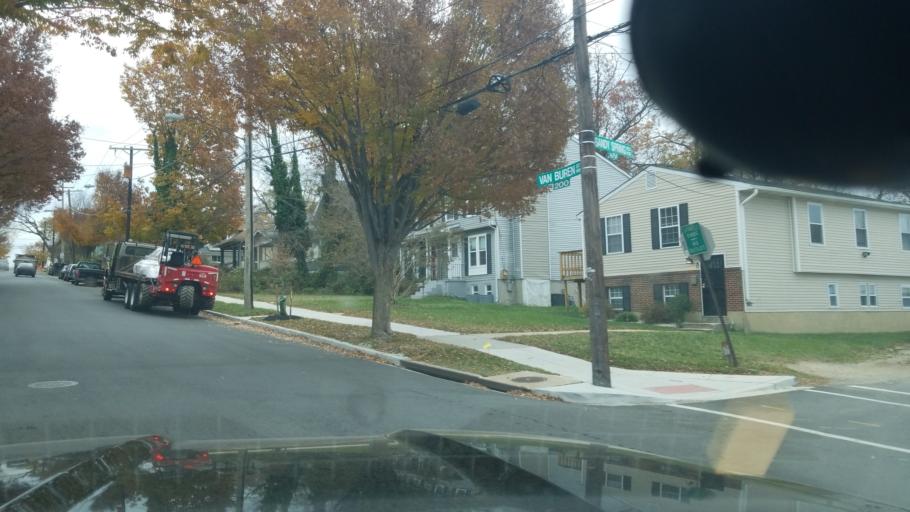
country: US
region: Maryland
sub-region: Montgomery County
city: Takoma Park
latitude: 38.9700
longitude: -77.0139
